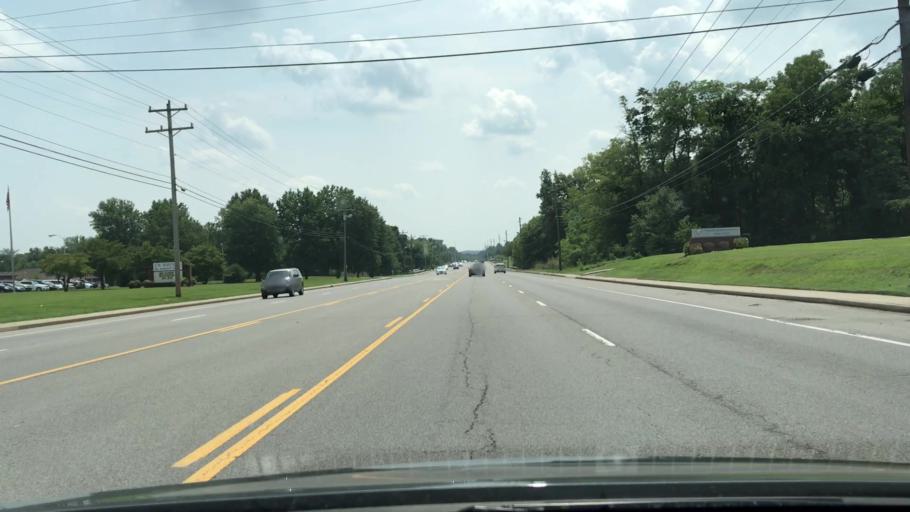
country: US
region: Tennessee
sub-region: Sumner County
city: Portland
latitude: 36.5567
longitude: -86.5086
